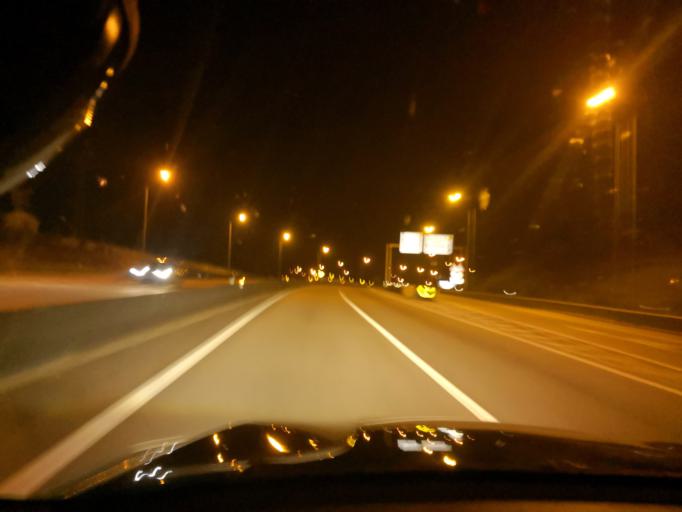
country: PT
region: Aveiro
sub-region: Albergaria-A-Velha
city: Albergaria-a-Velha
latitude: 40.6758
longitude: -8.4691
